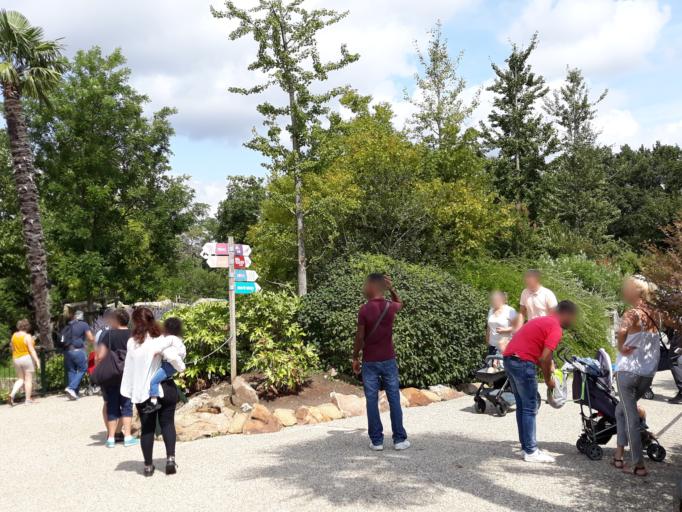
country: FR
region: Centre
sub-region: Departement du Loir-et-Cher
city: Saint-Aignan
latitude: 47.2443
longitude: 1.3478
